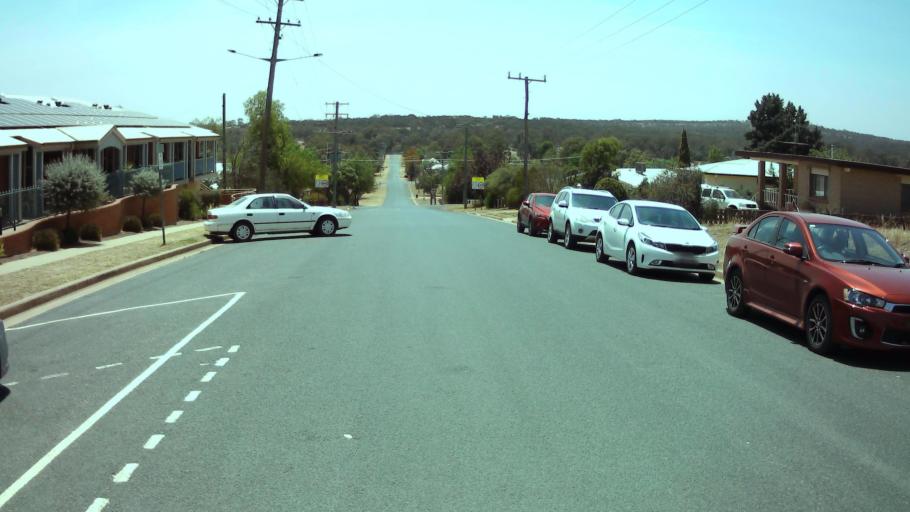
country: AU
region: New South Wales
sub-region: Weddin
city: Grenfell
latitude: -33.8945
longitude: 148.1683
